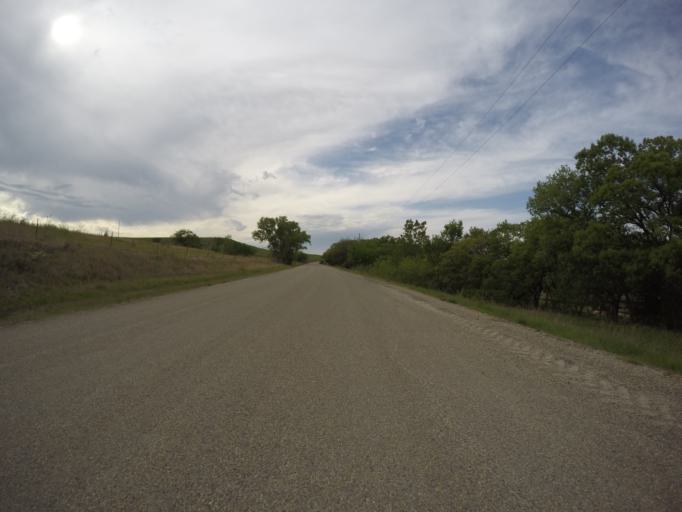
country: US
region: Kansas
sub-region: Riley County
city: Ogden
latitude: 39.0003
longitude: -96.5982
